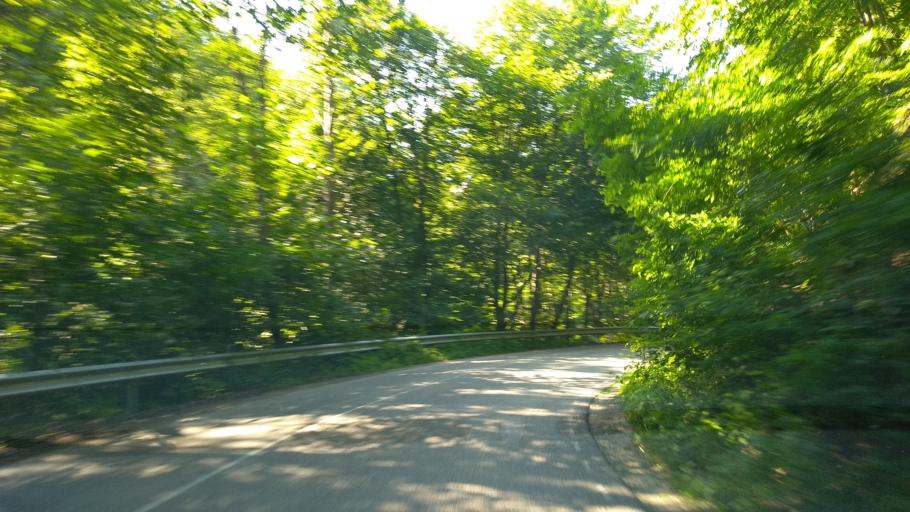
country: RO
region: Hunedoara
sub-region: Comuna Orastioara de Sus
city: Orastioara de Sus
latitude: 45.6437
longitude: 23.1957
